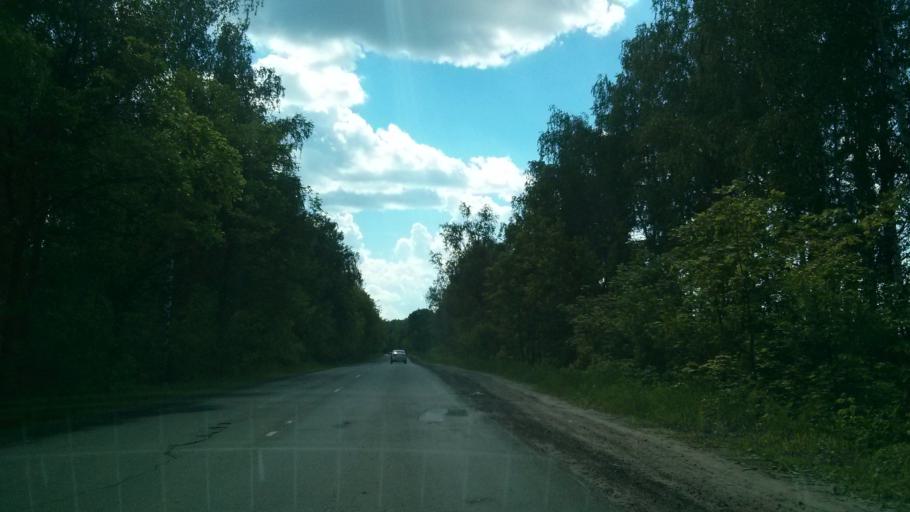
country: RU
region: Vladimir
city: Murom
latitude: 55.5479
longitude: 41.9955
